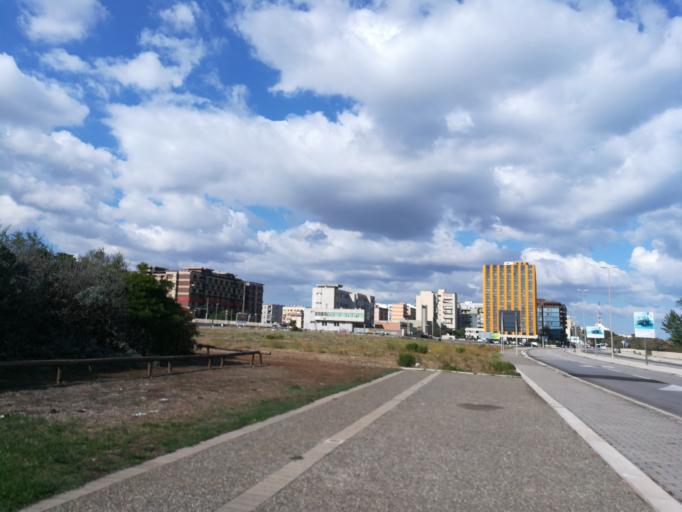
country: IT
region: Apulia
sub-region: Provincia di Bari
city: Bari
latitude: 41.1161
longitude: 16.8980
